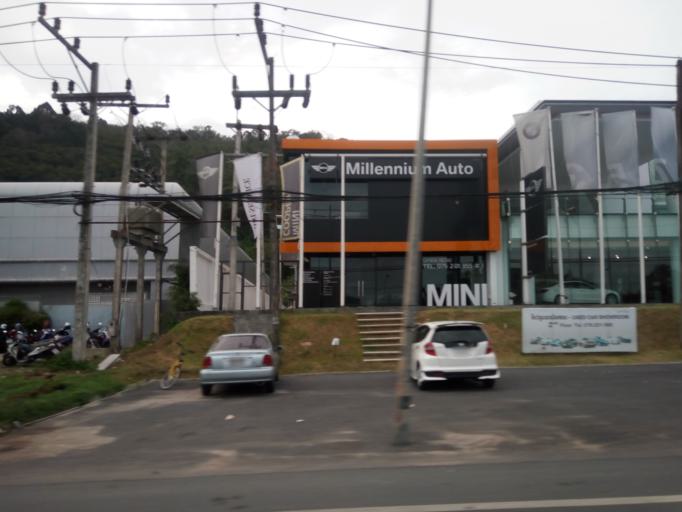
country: TH
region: Phuket
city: Wichit
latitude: 7.9175
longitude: 98.3694
